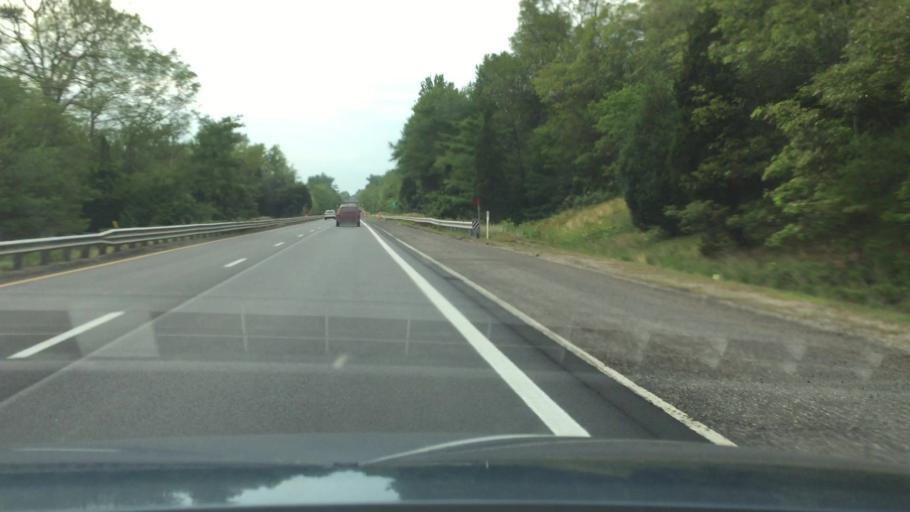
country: US
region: Massachusetts
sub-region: Plymouth County
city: Marshfield
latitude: 42.0744
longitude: -70.7342
